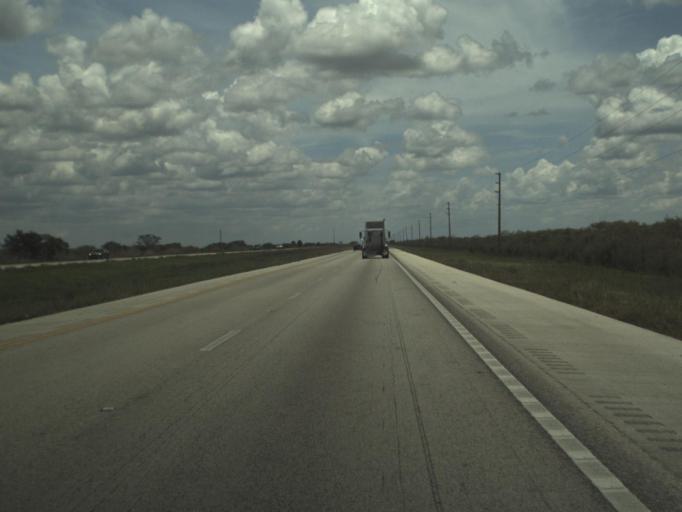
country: US
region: Florida
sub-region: Broward County
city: Weston
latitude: 26.1545
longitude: -80.7533
